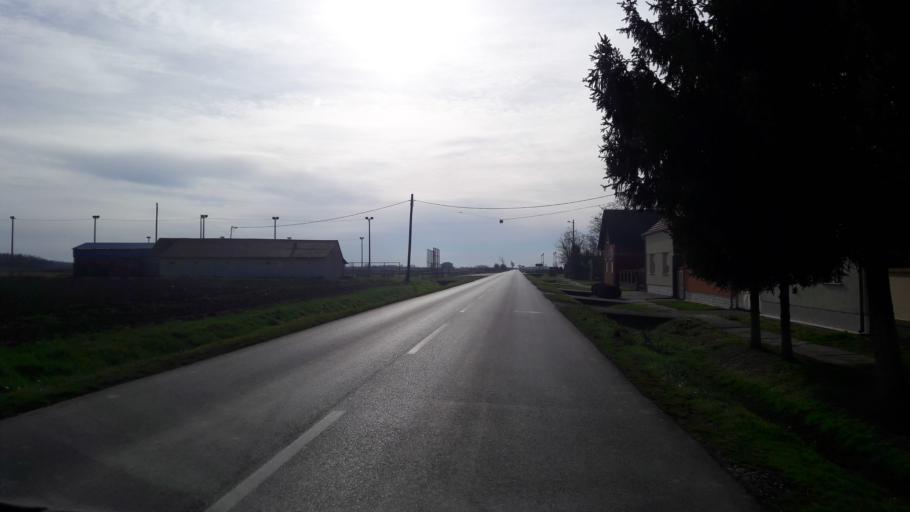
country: HR
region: Osjecko-Baranjska
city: Semeljci
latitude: 45.3443
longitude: 18.5575
